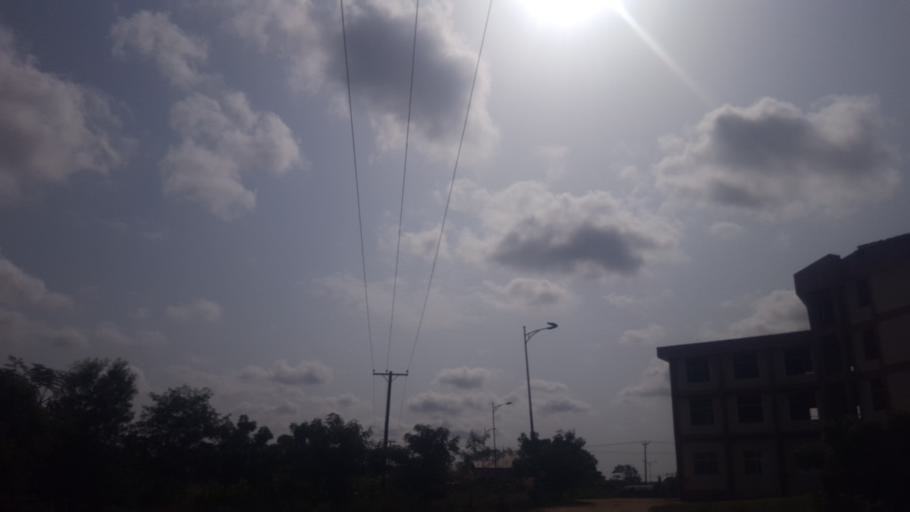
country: GH
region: Central
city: Winneba
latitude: 5.3751
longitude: -0.6417
